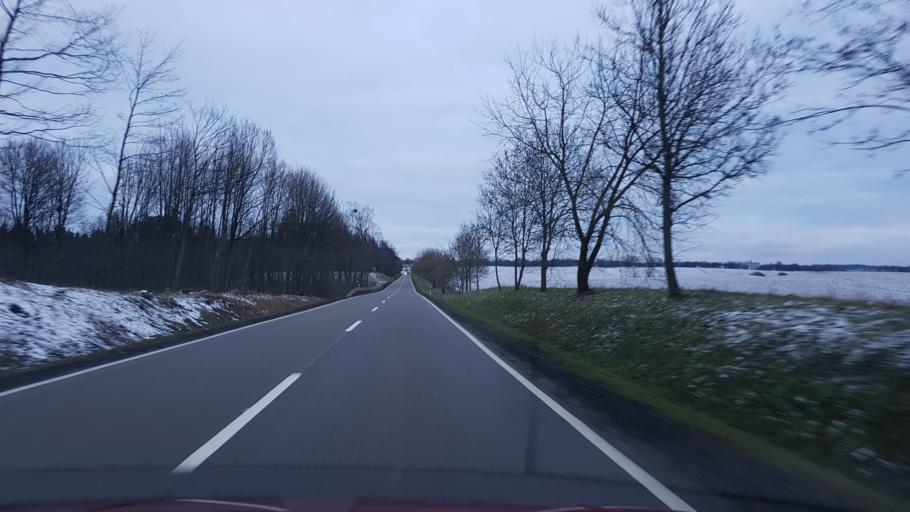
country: PL
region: Pomeranian Voivodeship
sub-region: Powiat czluchowski
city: Koczala
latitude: 54.0186
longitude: 17.1409
